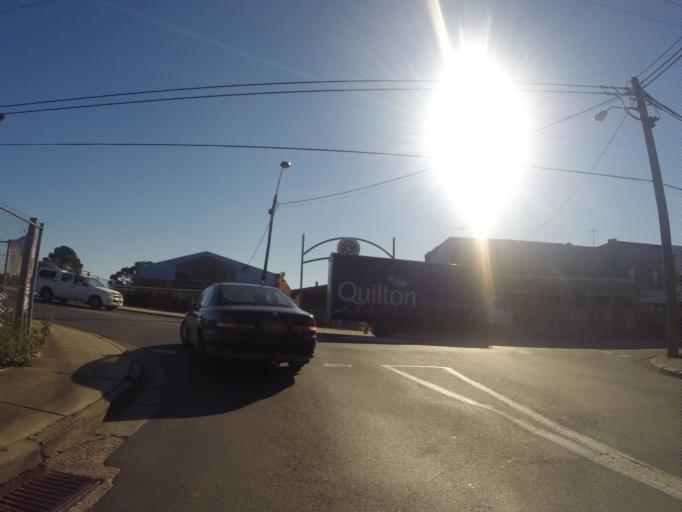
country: AU
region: New South Wales
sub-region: Bankstown
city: Regents Park
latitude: -33.8837
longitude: 151.0234
